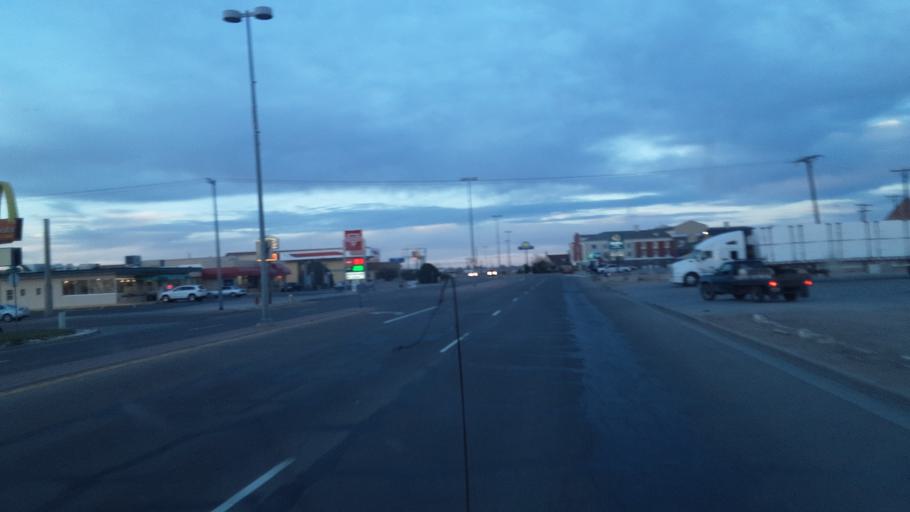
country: US
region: Colorado
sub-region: Prowers County
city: Lamar
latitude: 38.0994
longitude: -102.6187
